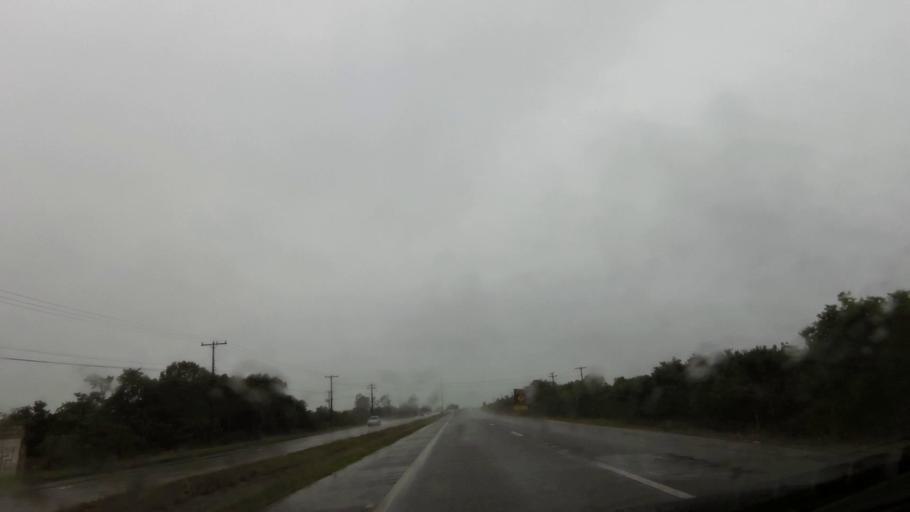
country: BR
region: Espirito Santo
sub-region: Guarapari
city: Guarapari
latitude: -20.5642
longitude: -40.4087
